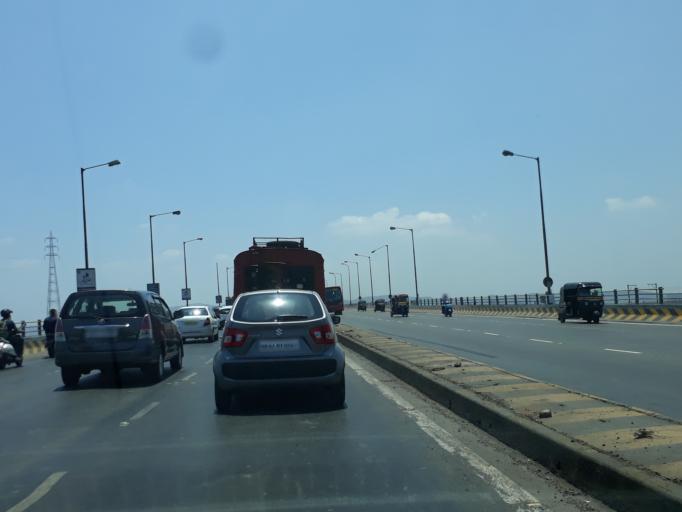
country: IN
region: Maharashtra
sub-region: Thane
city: Navi Mumbai
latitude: 19.0595
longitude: 72.9615
